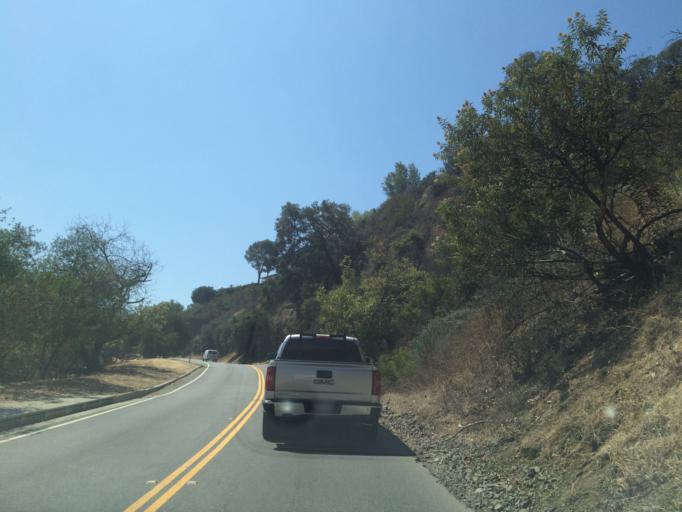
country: US
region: California
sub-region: Los Angeles County
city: Universal City
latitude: 34.1191
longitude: -118.3441
